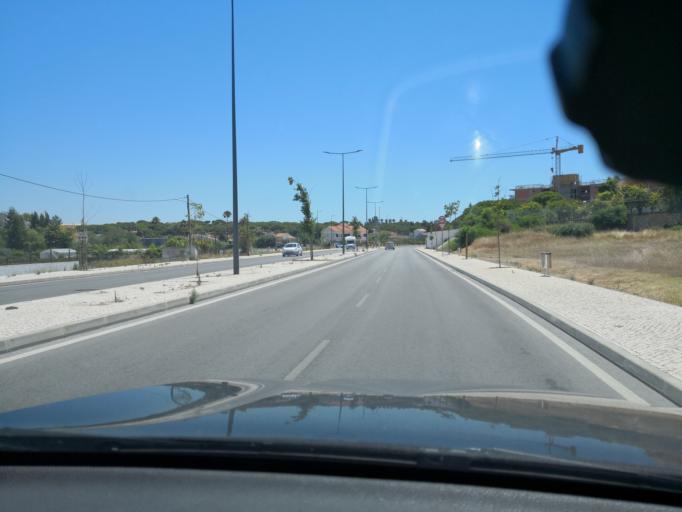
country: PT
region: Faro
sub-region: Loule
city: Quarteira
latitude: 37.0709
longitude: -8.0863
